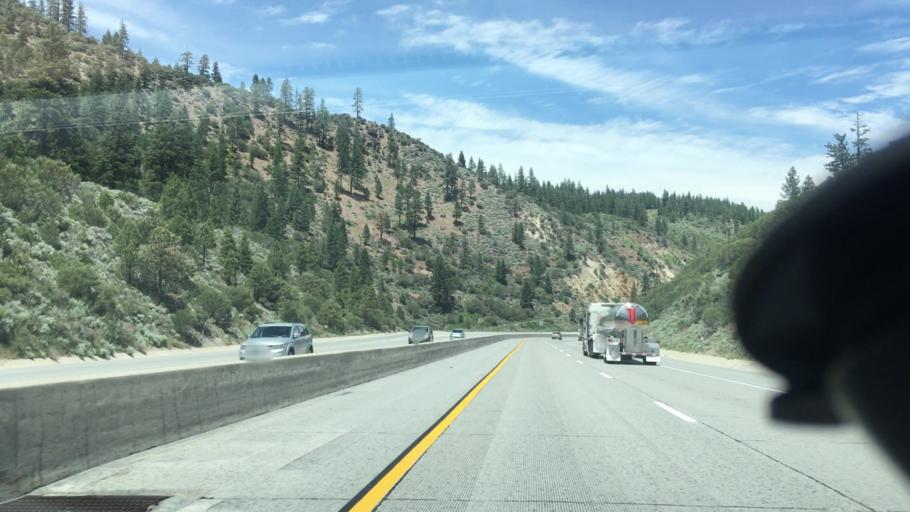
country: US
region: Nevada
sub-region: Washoe County
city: Verdi
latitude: 39.3907
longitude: -120.0250
